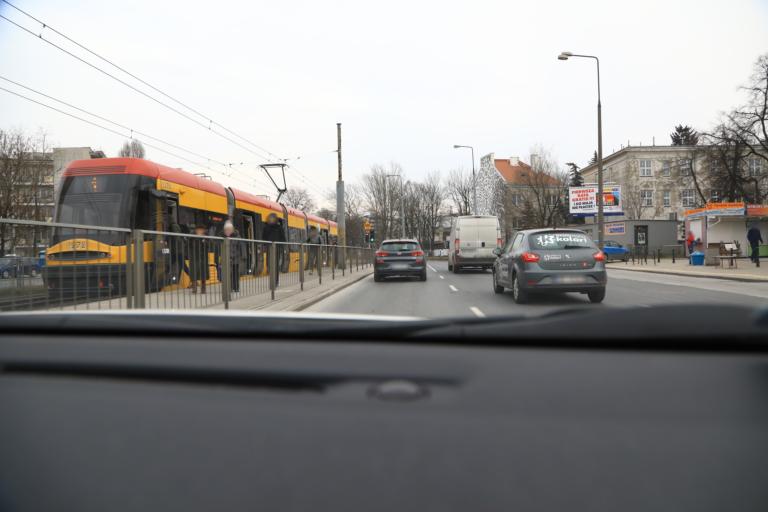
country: PL
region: Masovian Voivodeship
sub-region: Warszawa
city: Ochota
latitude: 52.2108
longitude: 20.9773
